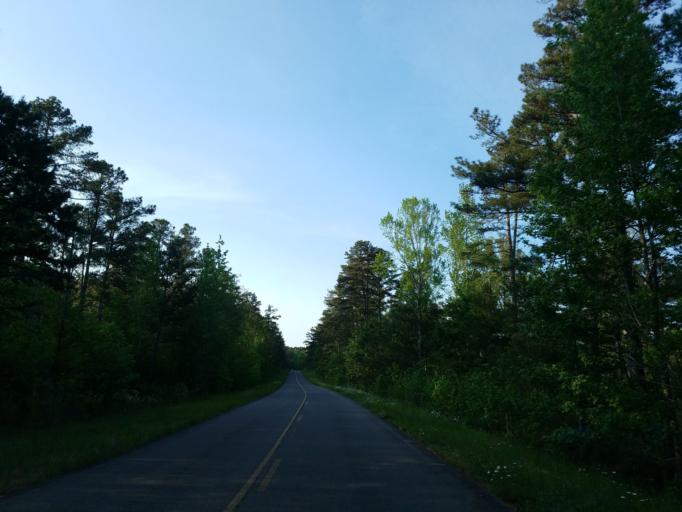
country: US
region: Georgia
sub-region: Gordon County
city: Calhoun
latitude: 34.6172
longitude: -85.0795
